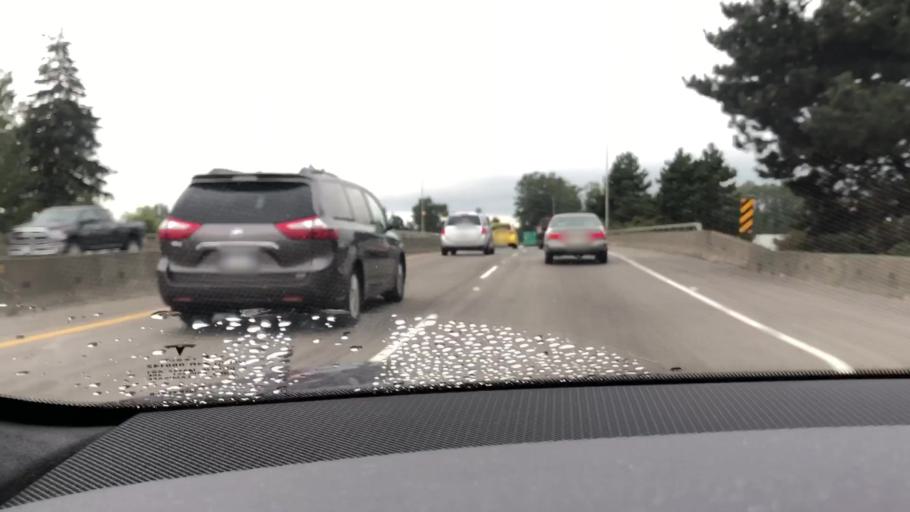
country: CA
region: British Columbia
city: New Westminster
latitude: 49.1829
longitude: -122.9564
